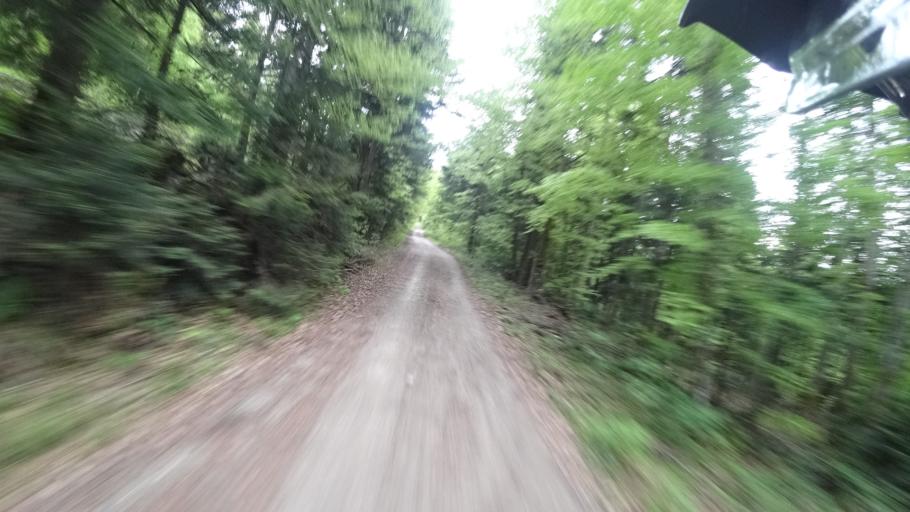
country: HR
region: Karlovacka
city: Plaski
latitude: 44.9161
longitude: 15.4276
